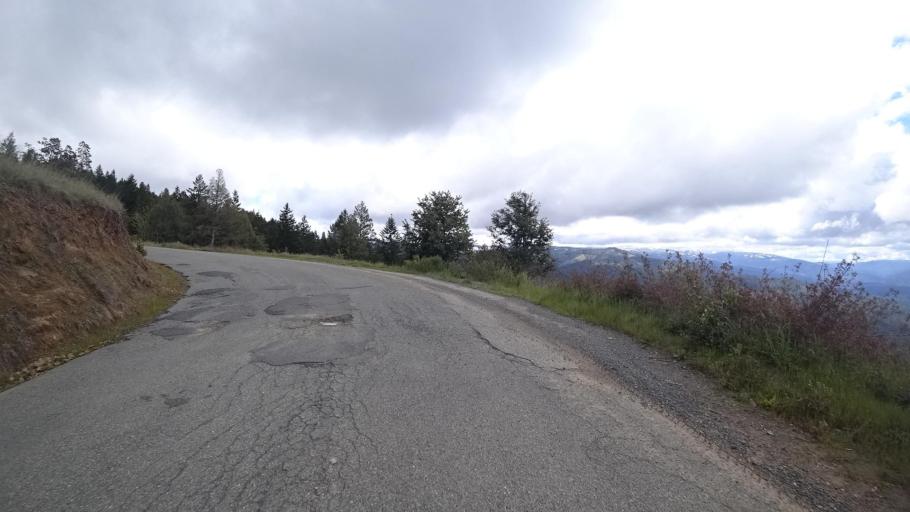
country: US
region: California
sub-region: Humboldt County
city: Blue Lake
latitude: 40.8580
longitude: -123.9100
